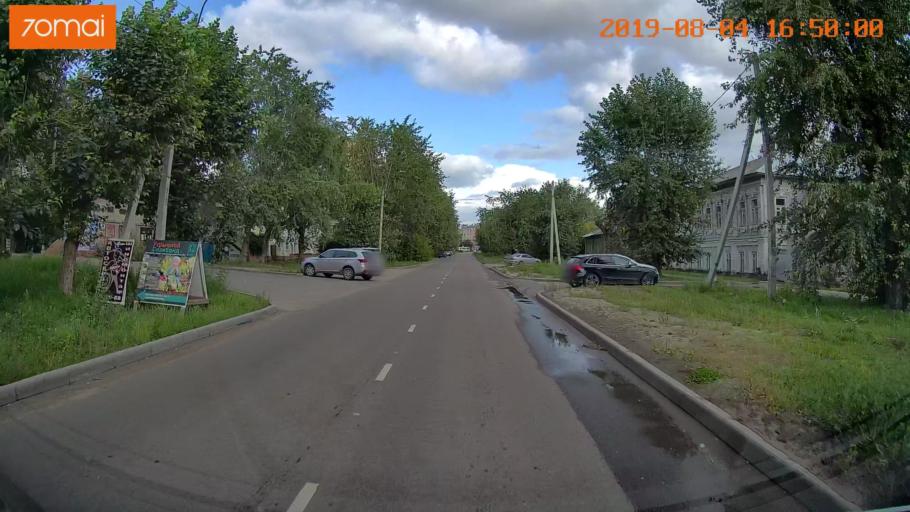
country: RU
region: Ivanovo
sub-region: Gorod Ivanovo
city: Ivanovo
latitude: 57.0159
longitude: 40.9651
